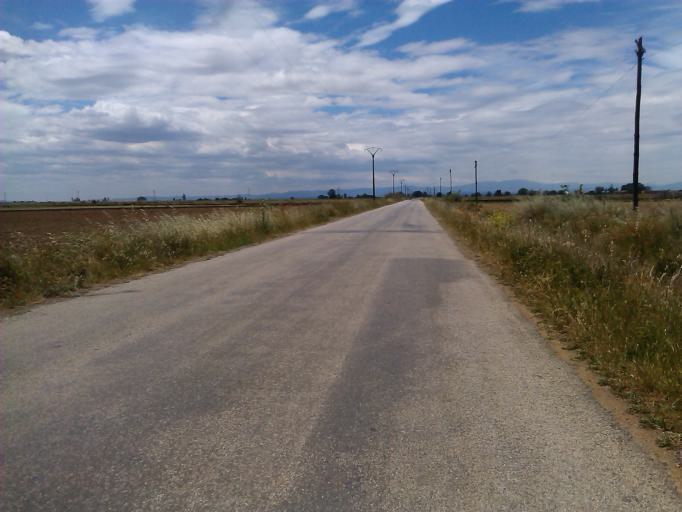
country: ES
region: Castille and Leon
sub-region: Provincia de Leon
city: Bustillo del Paramo
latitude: 42.4659
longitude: -5.7829
